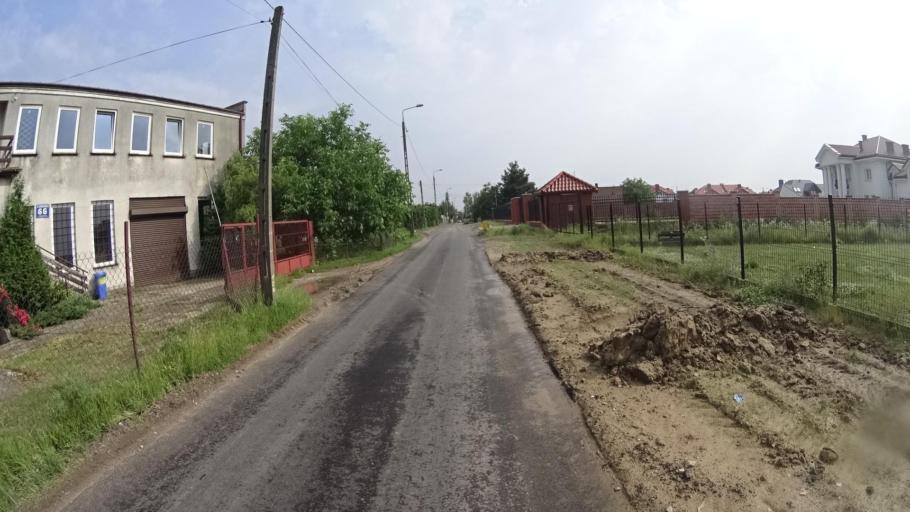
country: PL
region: Masovian Voivodeship
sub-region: Powiat pruszkowski
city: Raszyn
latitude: 52.1655
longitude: 20.9200
